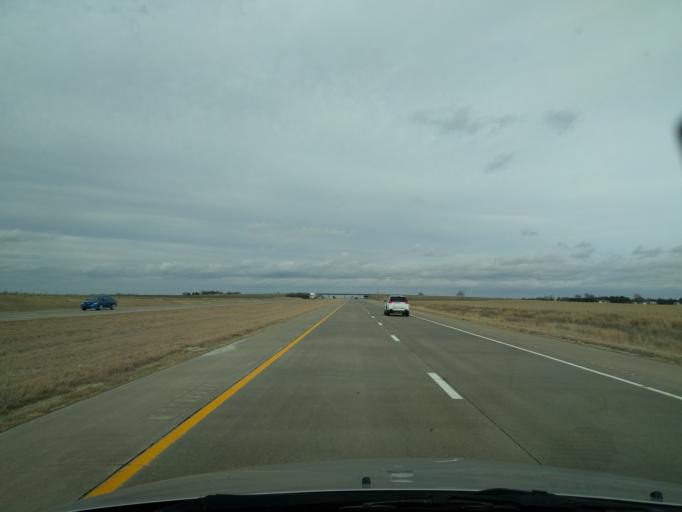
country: US
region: Kansas
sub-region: Saline County
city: Salina
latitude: 38.7043
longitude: -97.6218
